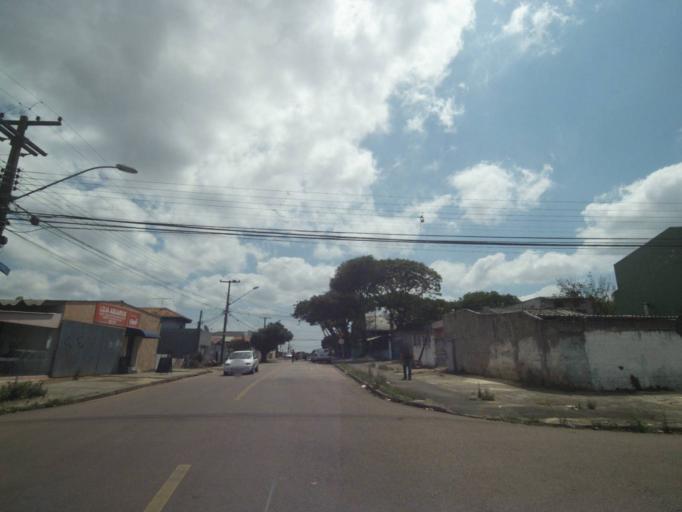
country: BR
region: Parana
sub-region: Curitiba
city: Curitiba
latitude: -25.5024
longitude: -49.3028
